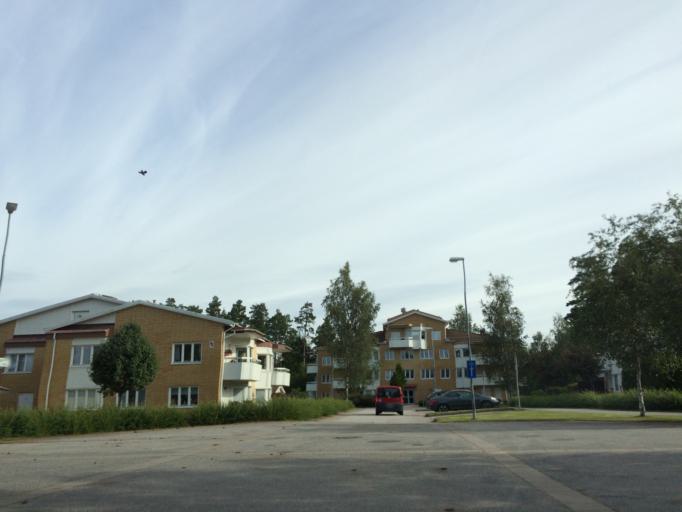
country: SE
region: Vaestra Goetaland
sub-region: Trollhattan
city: Trollhattan
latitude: 58.3221
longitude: 12.2742
